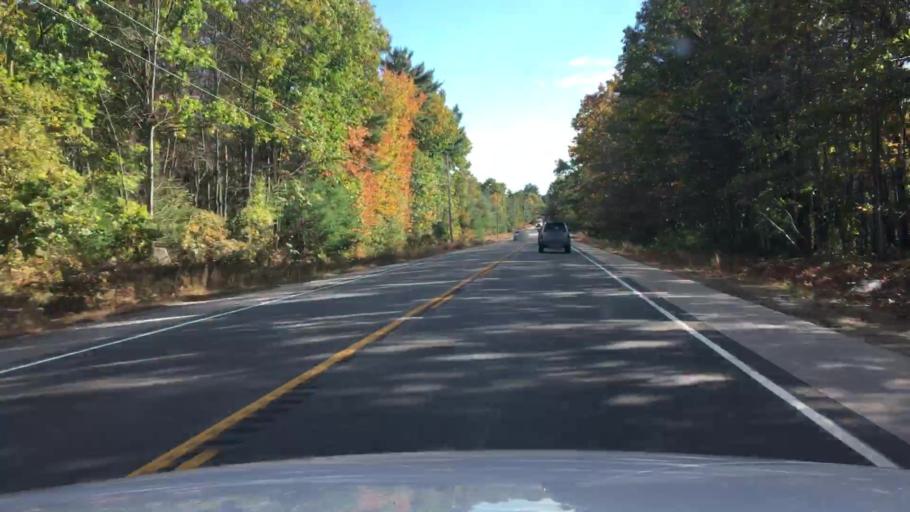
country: US
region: Maine
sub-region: York County
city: South Sanford
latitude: 43.3881
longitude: -70.6908
